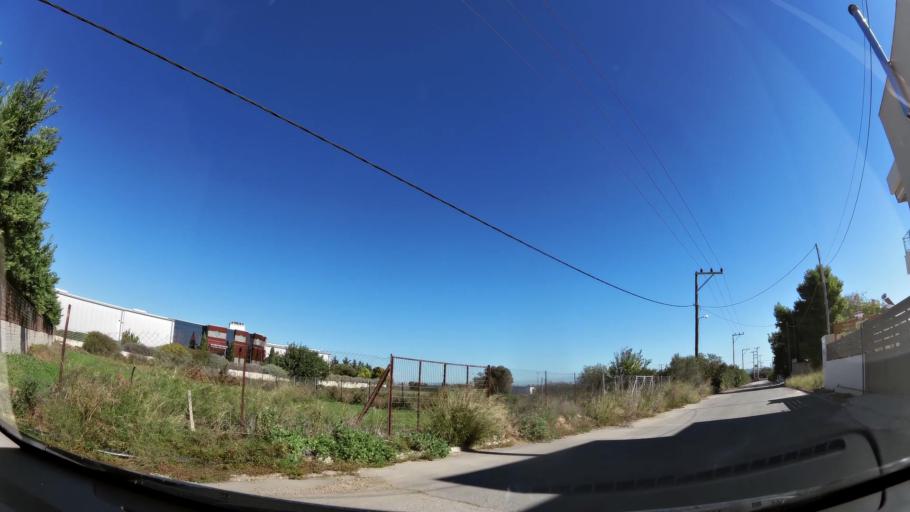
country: GR
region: Attica
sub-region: Nomarchia Anatolikis Attikis
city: Koropi
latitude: 37.9127
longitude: 23.8780
